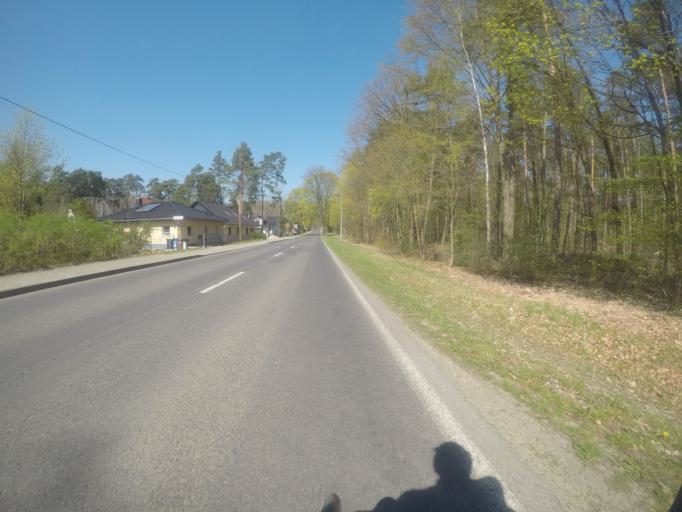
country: DE
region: Brandenburg
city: Rudnitz
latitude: 52.7539
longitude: 13.5658
